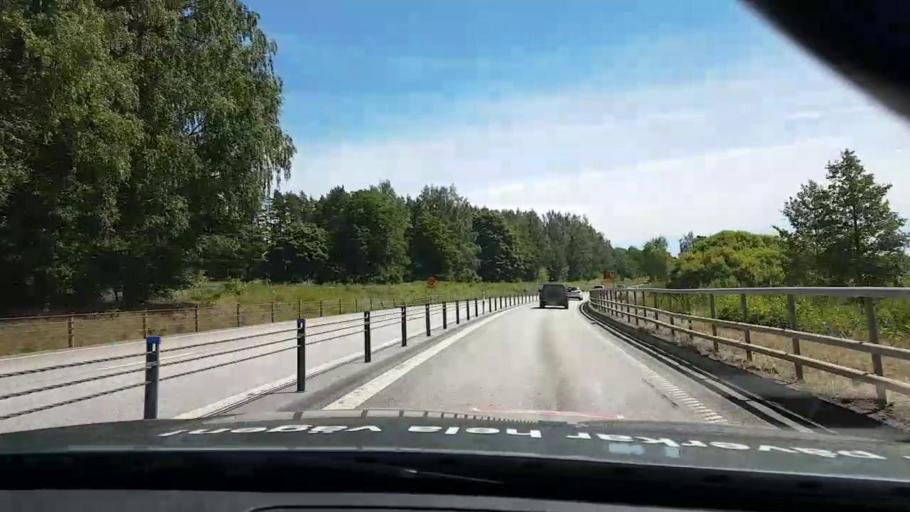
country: SE
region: Kalmar
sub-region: Vasterviks Kommun
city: Vaestervik
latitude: 57.8034
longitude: 16.5076
